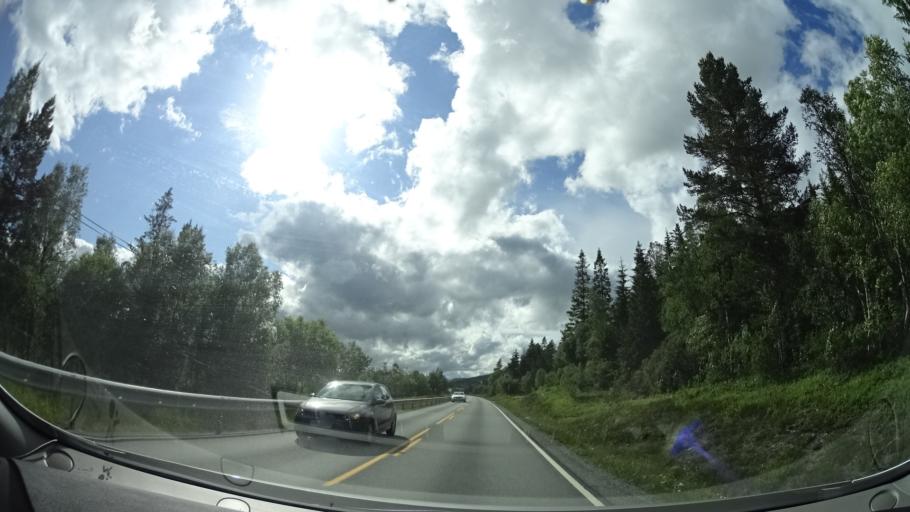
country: NO
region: Sor-Trondelag
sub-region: Snillfjord
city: Krokstadora
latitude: 63.2331
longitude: 9.4723
